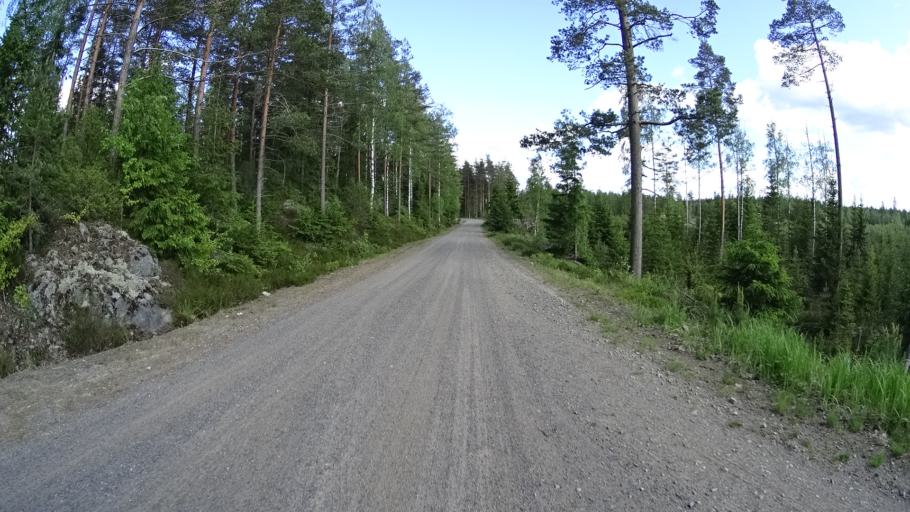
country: FI
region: Uusimaa
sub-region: Raaseporin
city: Pohja
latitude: 60.1560
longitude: 23.4893
